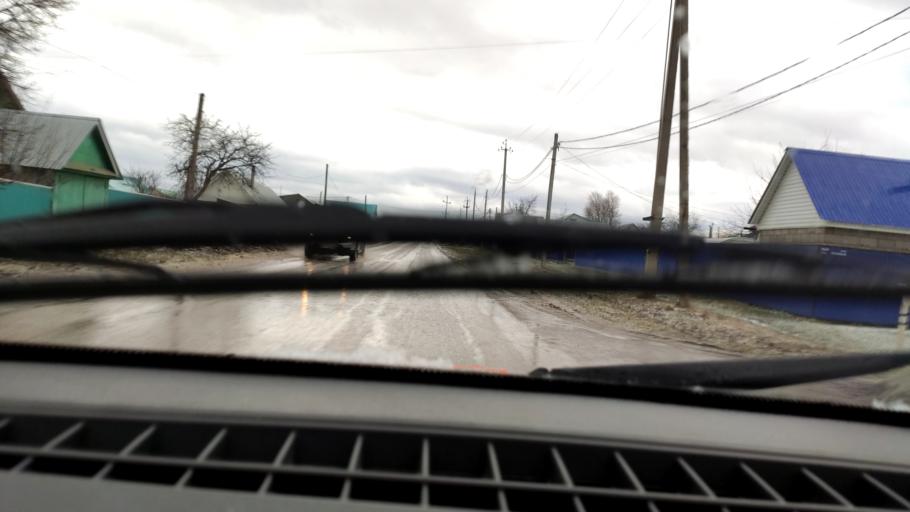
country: RU
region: Bashkortostan
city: Chekmagush
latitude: 55.1483
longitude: 54.6373
